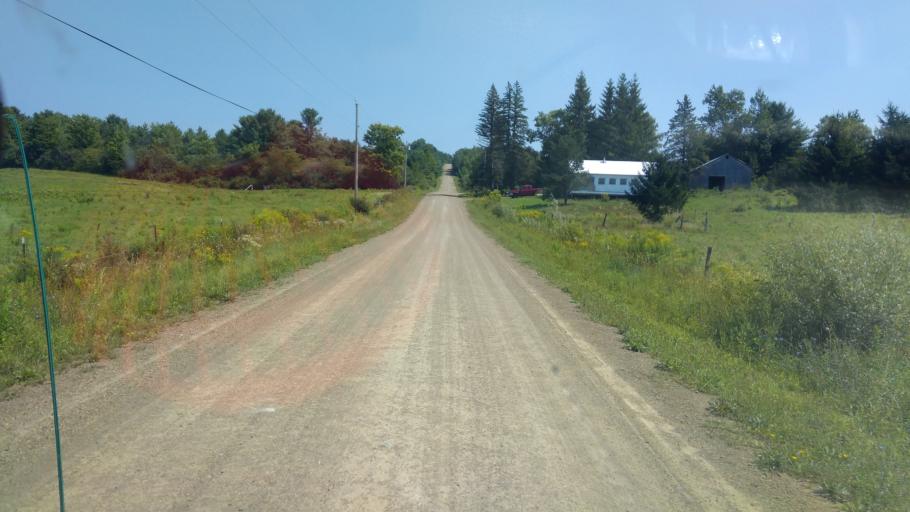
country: US
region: New York
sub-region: Allegany County
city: Belmont
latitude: 42.3903
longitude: -77.9650
